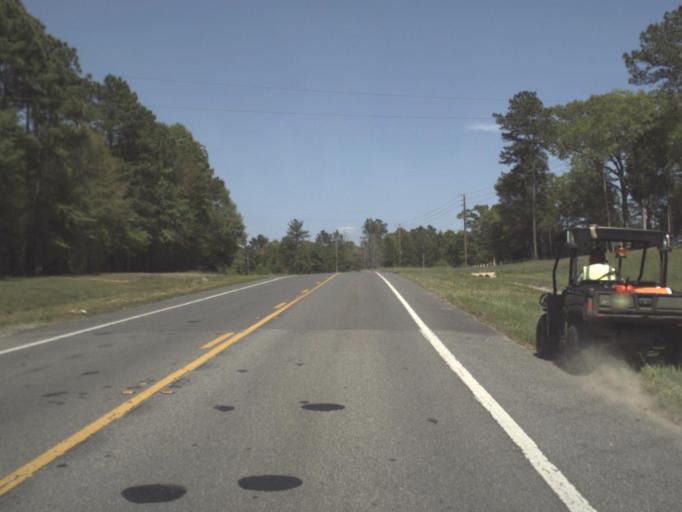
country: US
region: Florida
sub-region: Okaloosa County
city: Crestview
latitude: 30.7289
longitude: -86.6576
